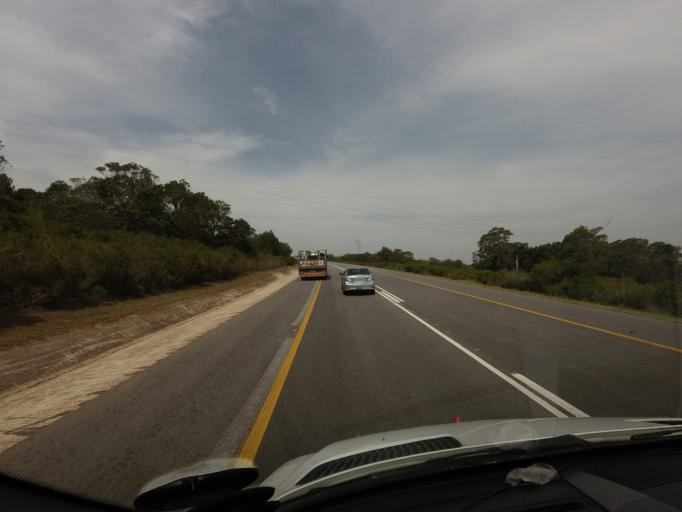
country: ZA
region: Eastern Cape
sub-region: Cacadu District Municipality
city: Kruisfontein
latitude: -33.9956
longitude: 24.7089
